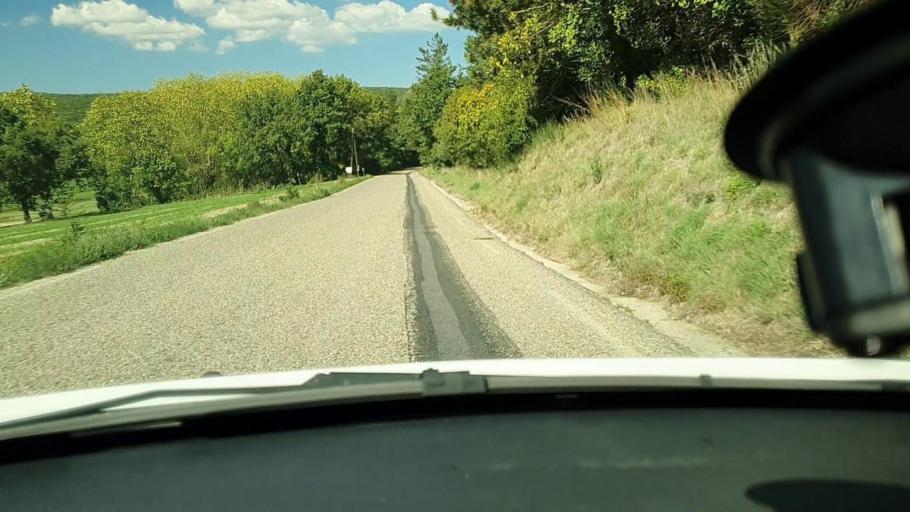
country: FR
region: Languedoc-Roussillon
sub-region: Departement du Gard
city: Goudargues
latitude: 44.1424
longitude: 4.4497
